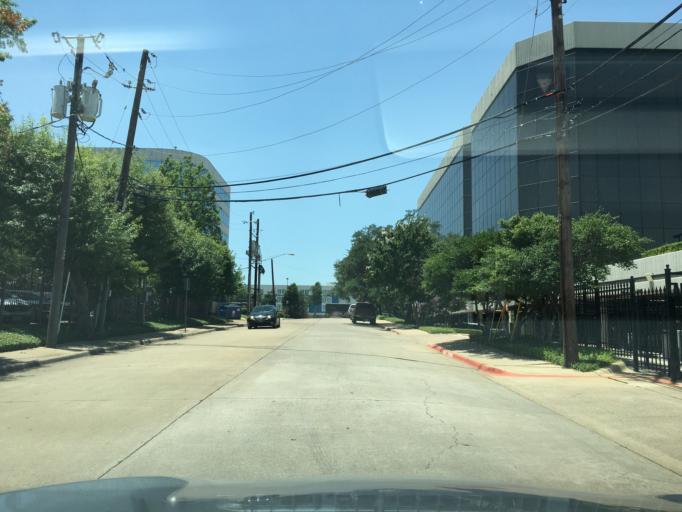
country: US
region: Texas
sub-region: Dallas County
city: University Park
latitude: 32.8851
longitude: -96.7682
